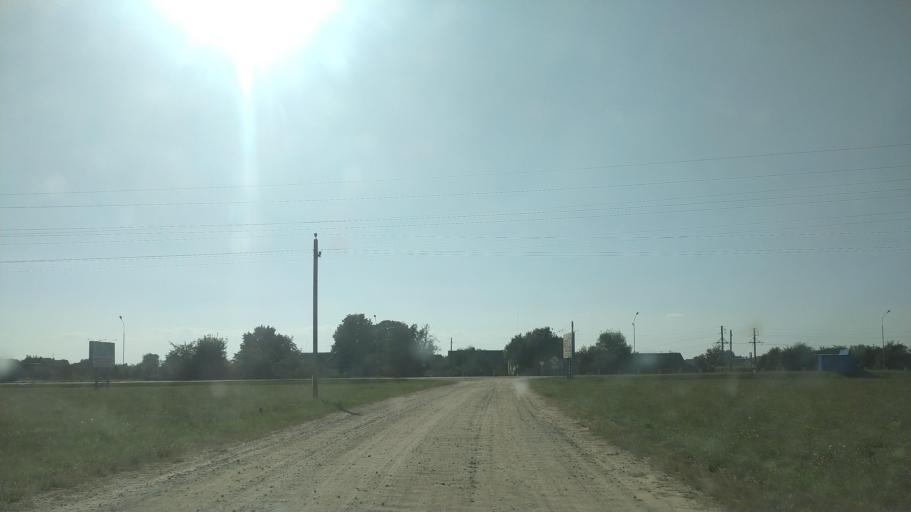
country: BY
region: Brest
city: Byaroza
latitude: 52.5132
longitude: 24.9692
